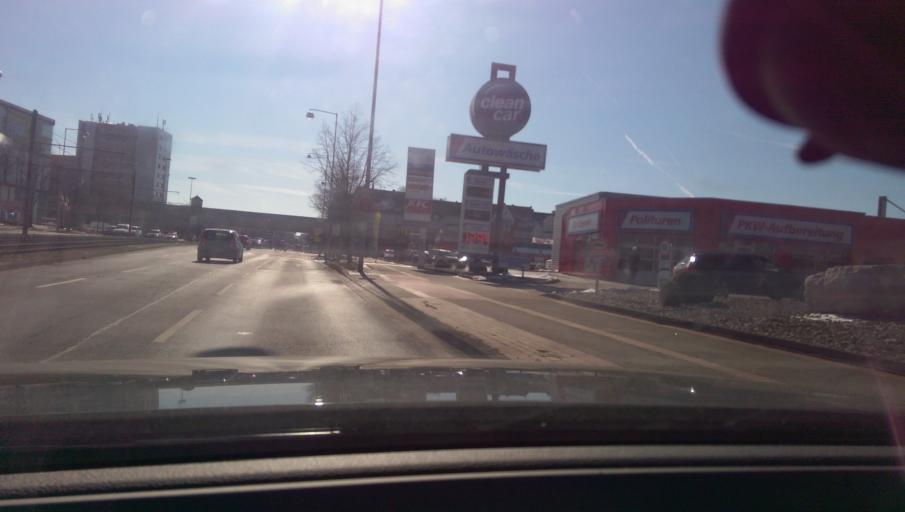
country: DE
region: Lower Saxony
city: Hannover
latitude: 52.3441
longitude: 9.7632
